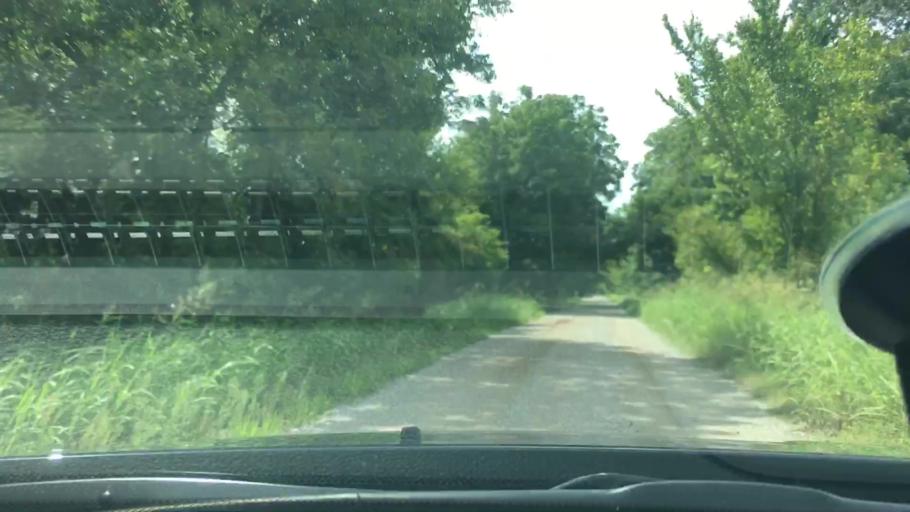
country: US
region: Oklahoma
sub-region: Garvin County
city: Stratford
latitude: 34.8256
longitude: -97.0572
